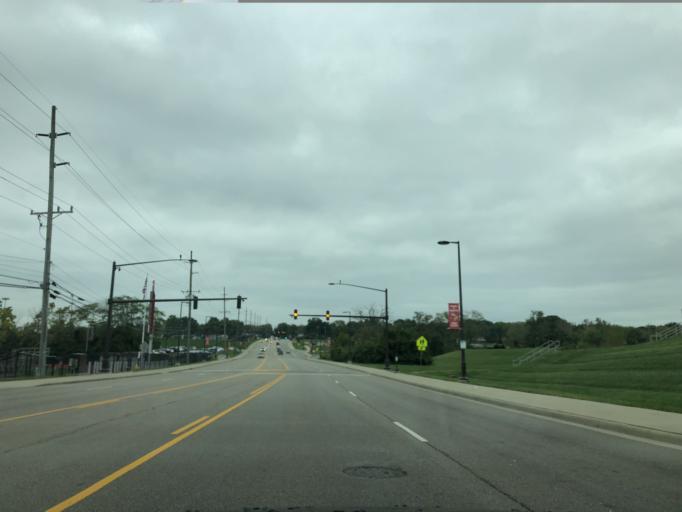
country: US
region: Ohio
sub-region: Hamilton County
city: Glendale
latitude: 39.2757
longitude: -84.4441
